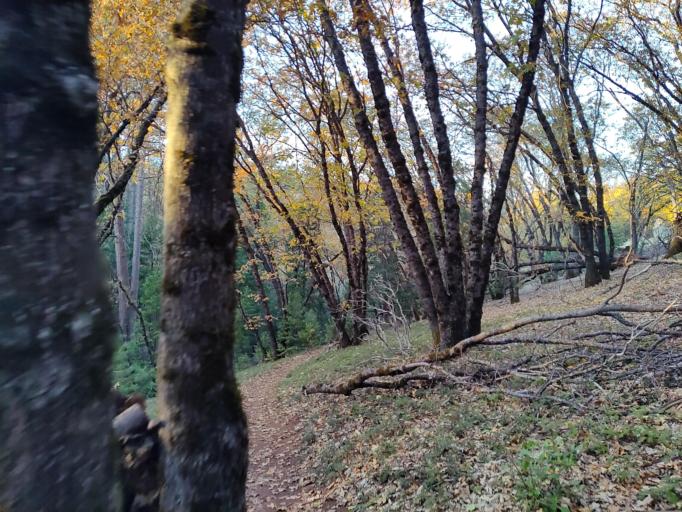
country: US
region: California
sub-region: Placer County
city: Meadow Vista
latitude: 39.0346
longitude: -120.9871
